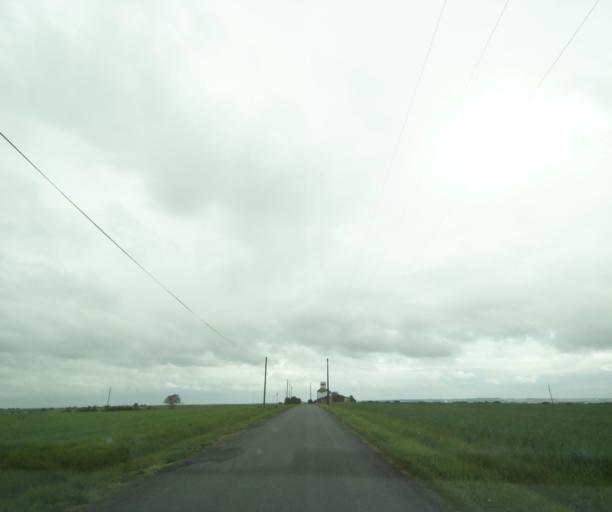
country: FR
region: Poitou-Charentes
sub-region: Departement de la Charente-Maritime
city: Perignac
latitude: 45.6569
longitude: -0.5057
